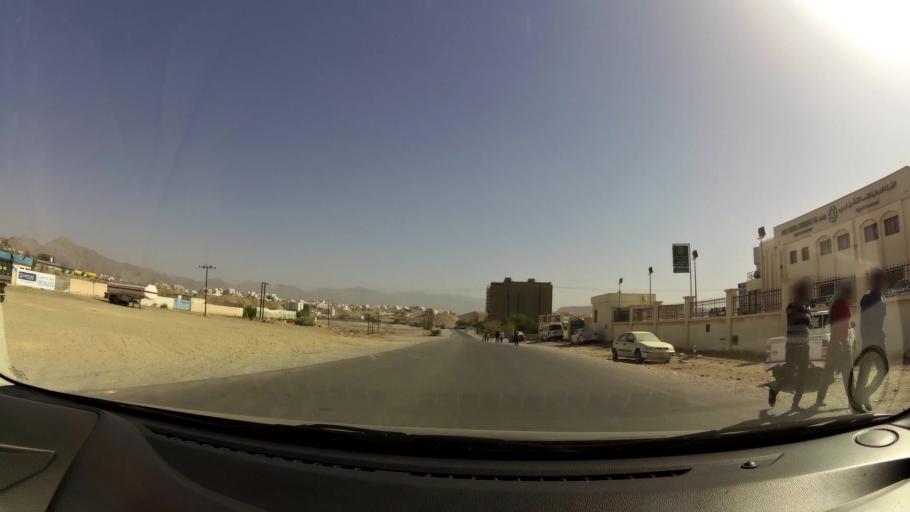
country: OM
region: Muhafazat Masqat
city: Bawshar
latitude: 23.5681
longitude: 58.3485
